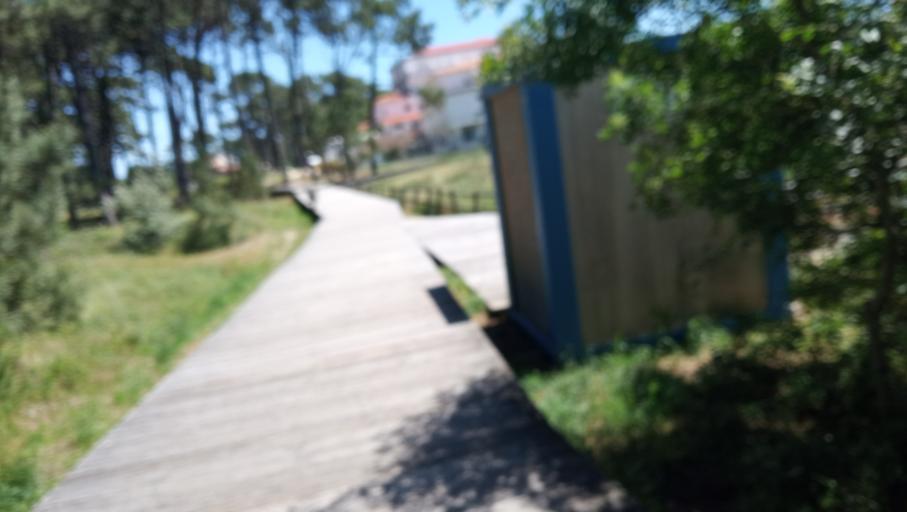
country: ES
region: Galicia
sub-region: Provincia de Pontevedra
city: A Guarda
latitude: 41.8730
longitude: -8.8706
